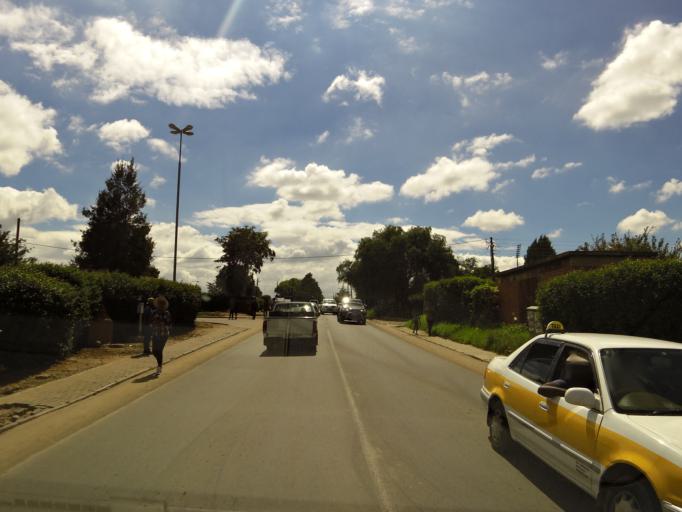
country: LS
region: Maseru
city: Maseru
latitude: -29.3107
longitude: 27.4960
